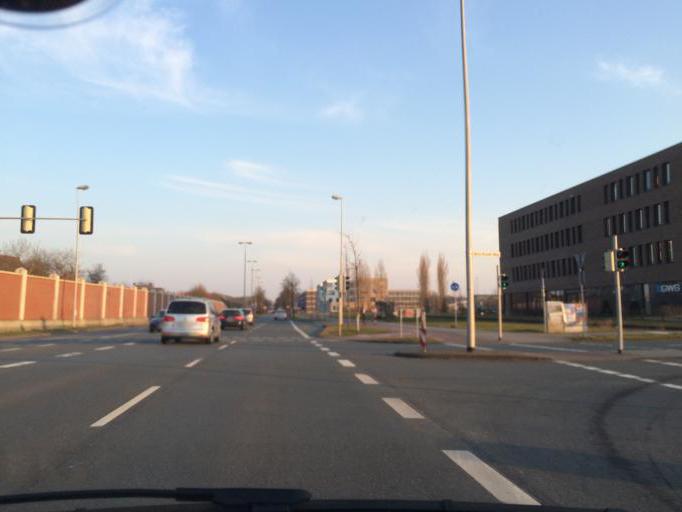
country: DE
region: North Rhine-Westphalia
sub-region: Regierungsbezirk Munster
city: Muenster
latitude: 51.9389
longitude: 7.6528
